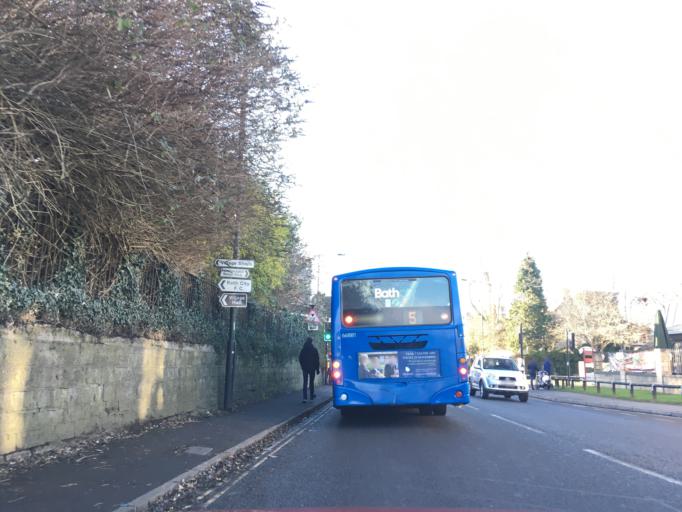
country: GB
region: England
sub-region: Bath and North East Somerset
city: Bath
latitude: 51.3803
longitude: -2.3897
